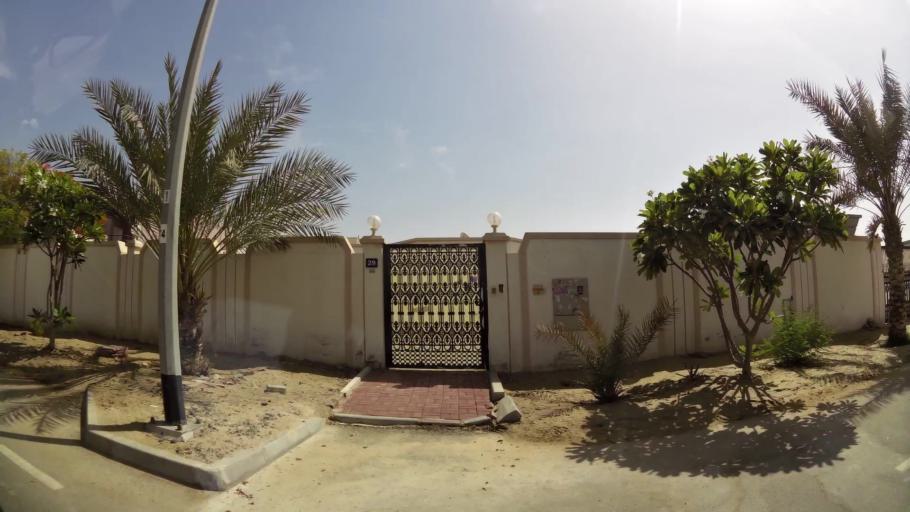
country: AE
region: Ash Shariqah
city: Sharjah
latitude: 25.2025
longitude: 55.4253
